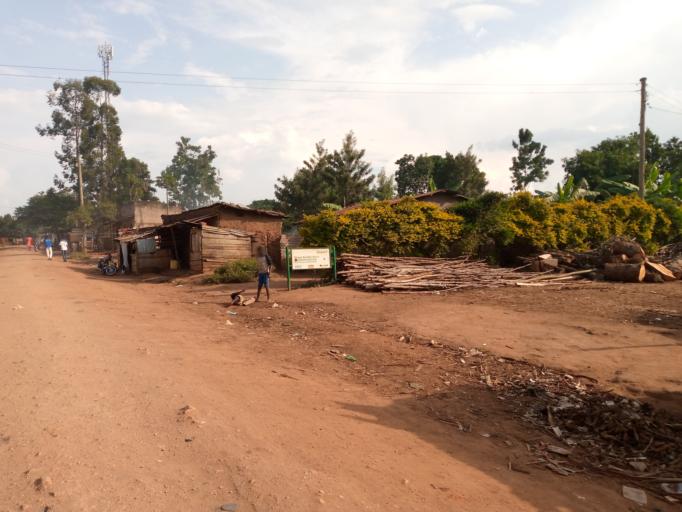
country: UG
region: Eastern Region
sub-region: Mbale District
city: Mbale
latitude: 1.0624
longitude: 34.1544
